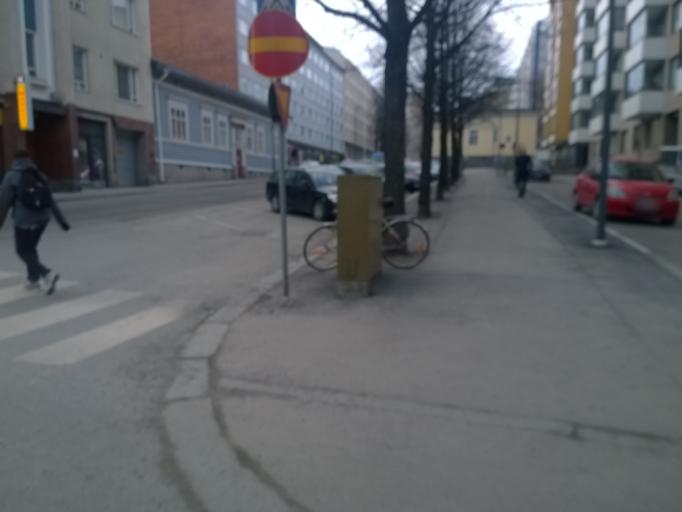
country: FI
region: Pirkanmaa
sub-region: Tampere
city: Tampere
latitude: 61.4949
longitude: 23.7559
